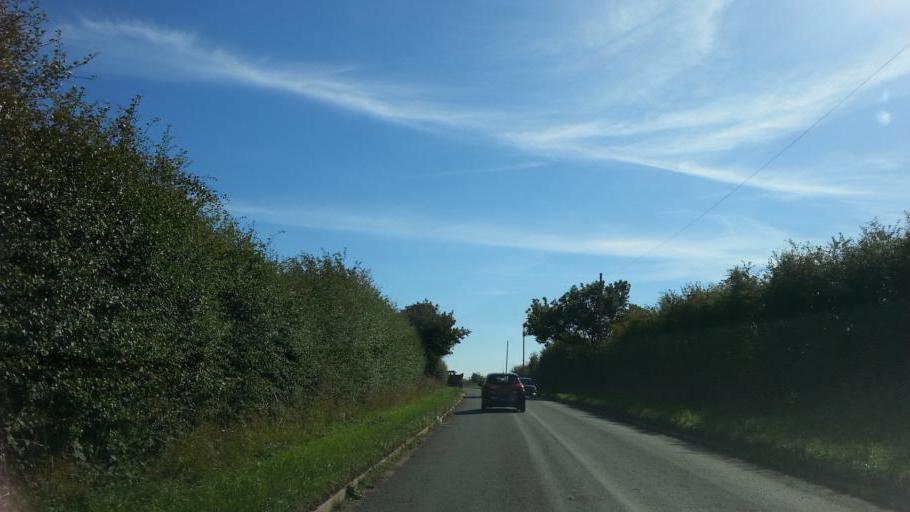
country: GB
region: England
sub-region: Staffordshire
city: Stafford
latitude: 52.7928
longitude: -2.1611
